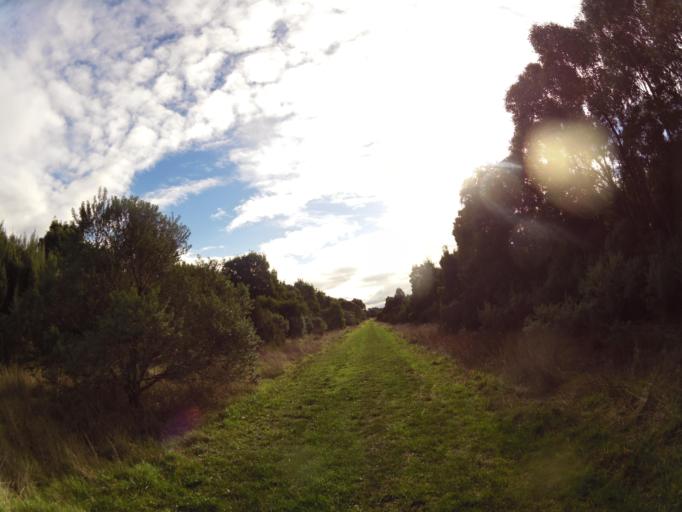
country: AU
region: Victoria
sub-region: Bass Coast
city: North Wonthaggi
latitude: -38.6214
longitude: 145.5744
